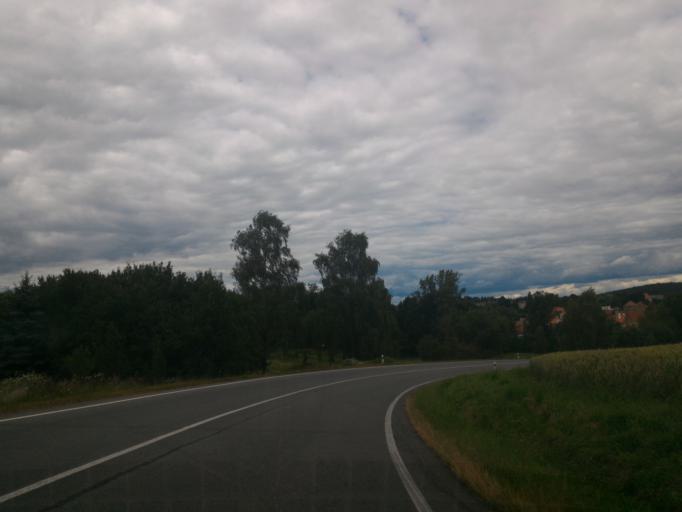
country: CZ
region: Vysocina
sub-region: Okres Pelhrimov
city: Zeliv
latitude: 49.5064
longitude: 15.1780
